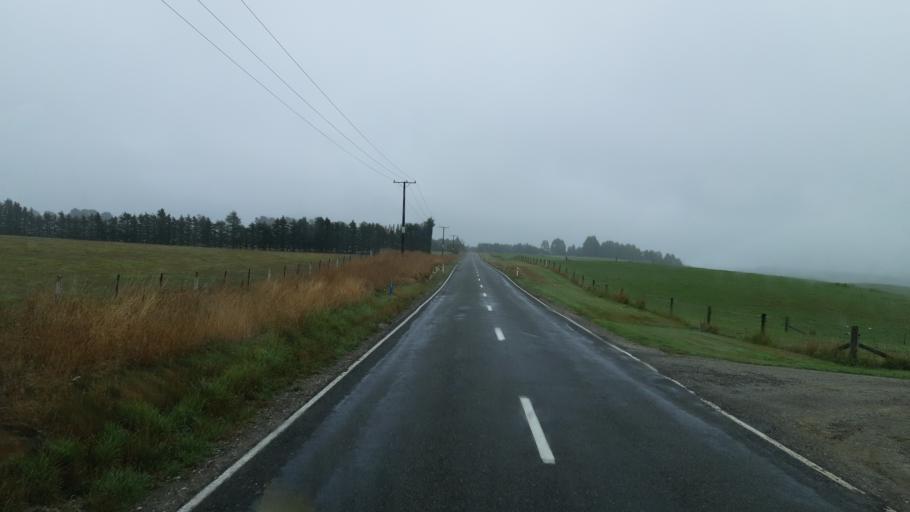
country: NZ
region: Otago
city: Oamaru
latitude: -44.9281
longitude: 170.8000
